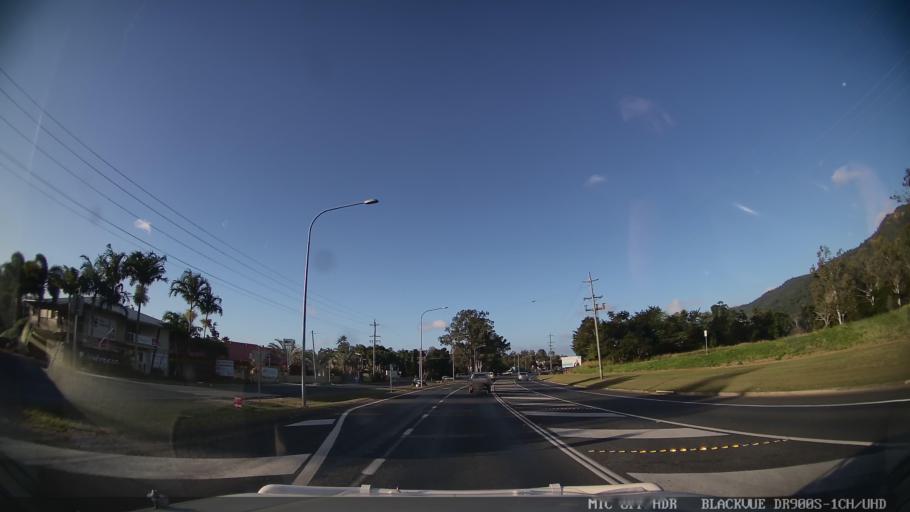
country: AU
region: Queensland
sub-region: Whitsunday
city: Proserpine
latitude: -20.2878
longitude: 148.6785
